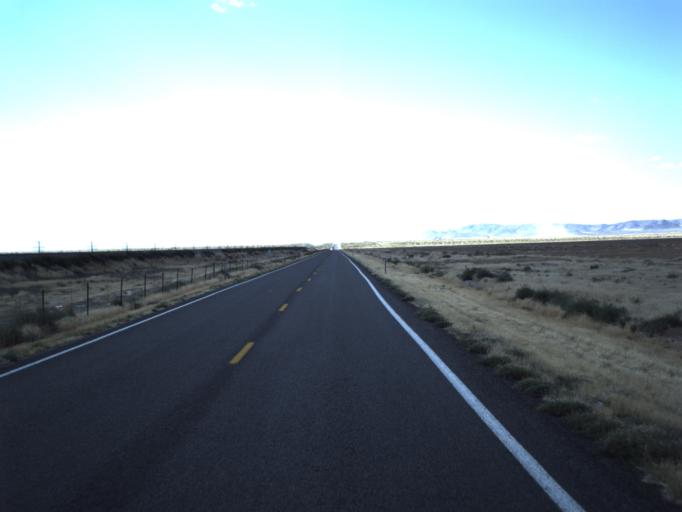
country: US
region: Utah
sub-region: Millard County
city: Delta
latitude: 38.9734
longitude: -112.7981
